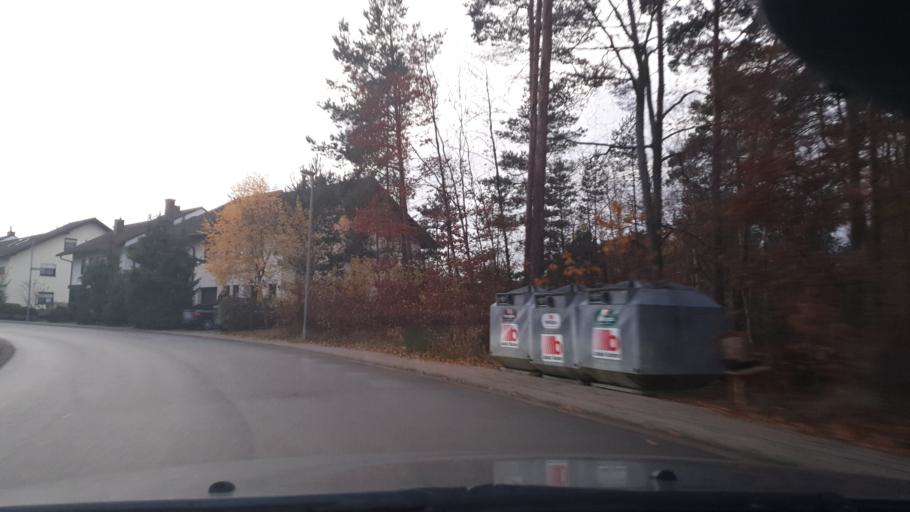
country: DE
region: Rheinland-Pfalz
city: Kaiserslautern
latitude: 49.4250
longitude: 7.7381
